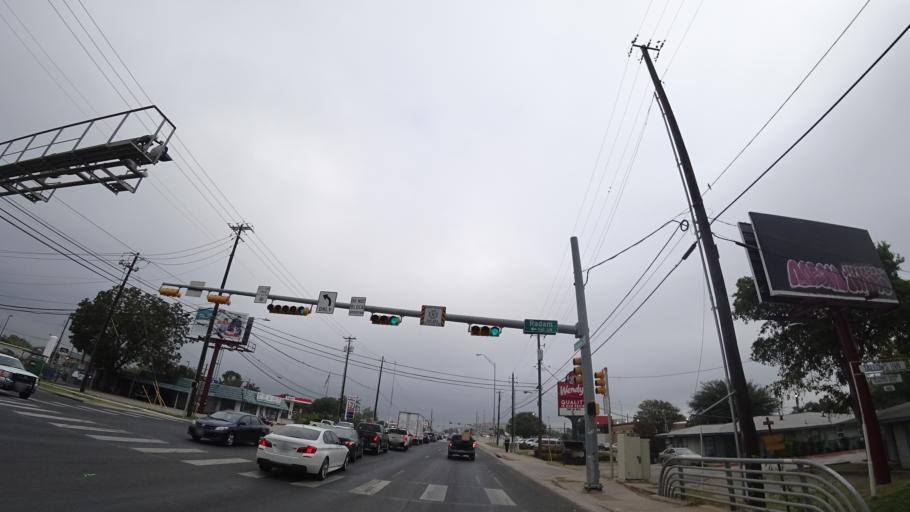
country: US
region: Texas
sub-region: Travis County
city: Austin
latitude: 30.2212
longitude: -97.7649
